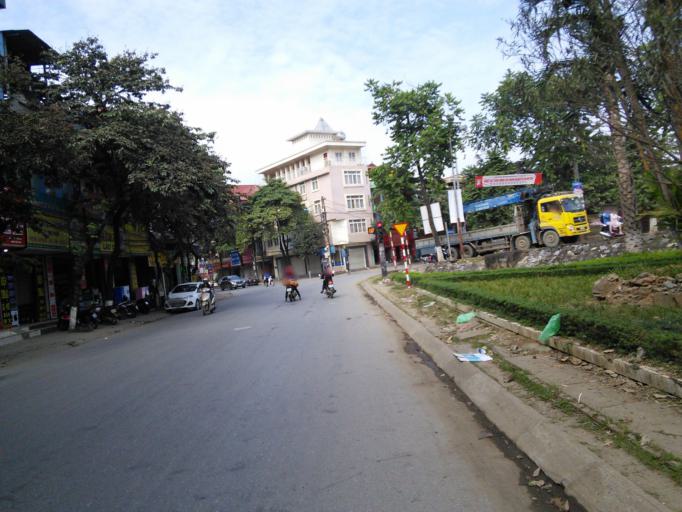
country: VN
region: Lao Cai
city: Lao Cai
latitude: 22.4746
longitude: 103.9731
